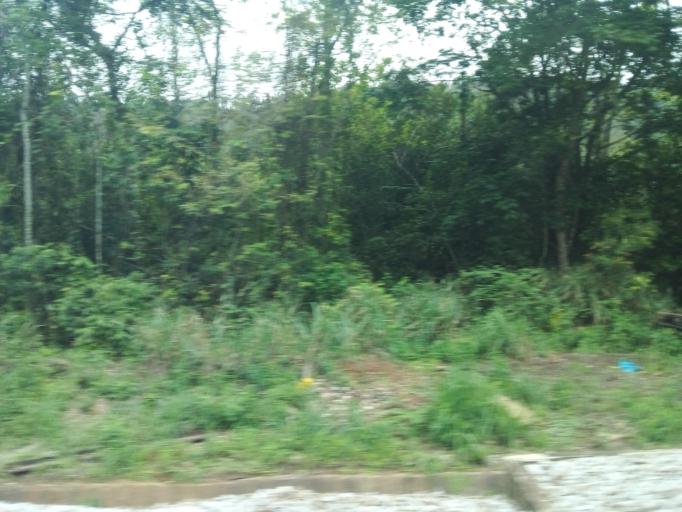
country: BR
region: Minas Gerais
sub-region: Rio Piracicaba
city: Rio Piracicaba
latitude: -19.9702
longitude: -43.2299
